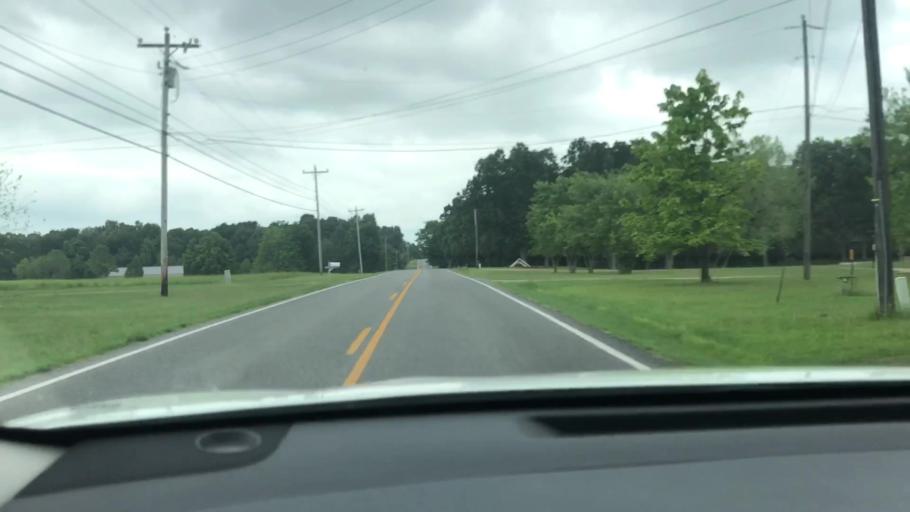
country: US
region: Kentucky
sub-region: Calloway County
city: Murray
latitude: 36.6831
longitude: -88.2997
